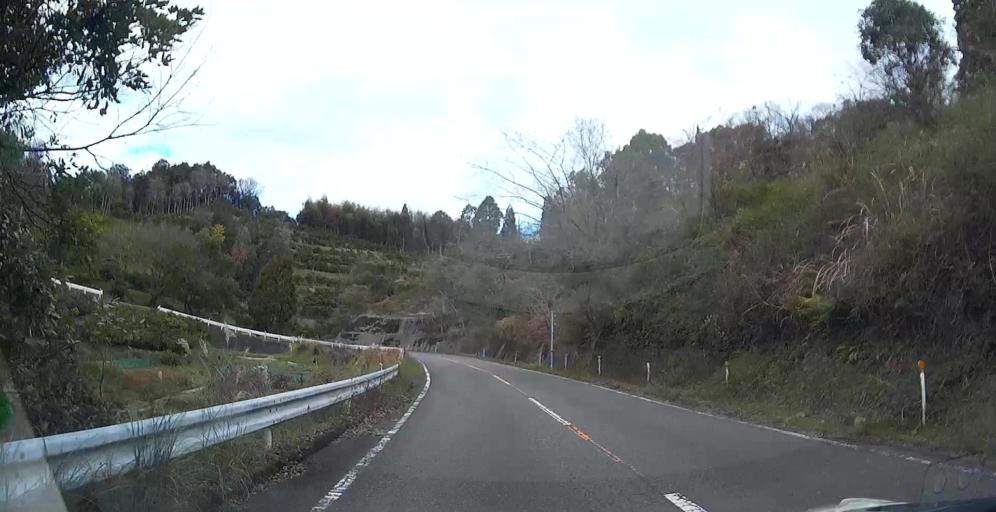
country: JP
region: Kumamoto
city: Yatsushiro
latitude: 32.3667
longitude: 130.5068
